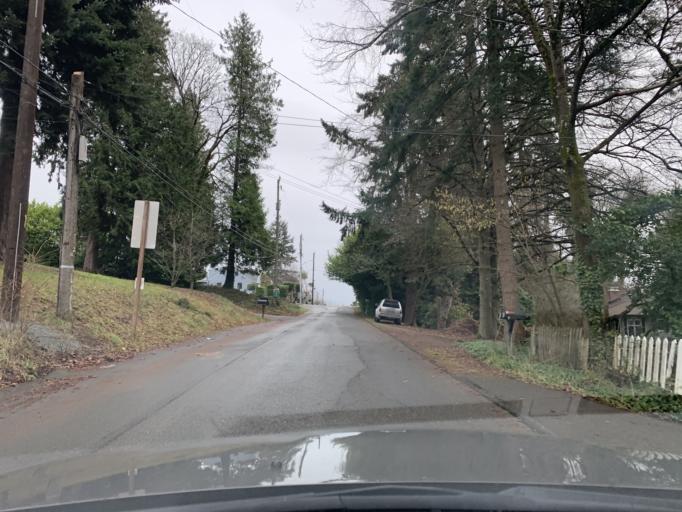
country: US
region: Washington
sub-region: King County
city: Tukwila
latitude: 47.4686
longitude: -122.2750
